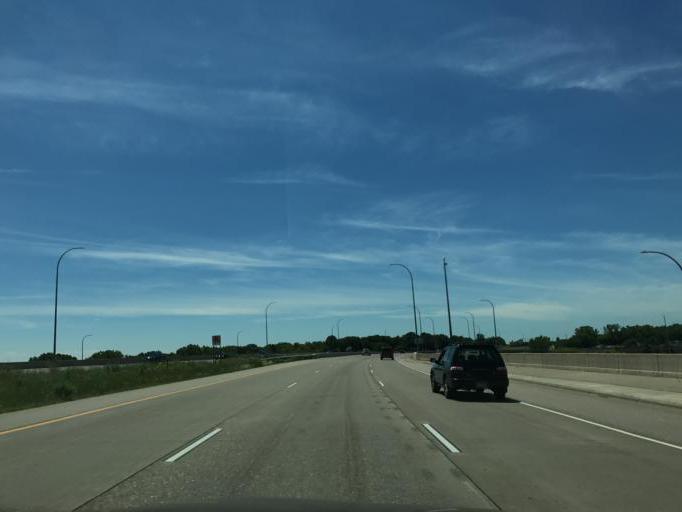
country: US
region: Minnesota
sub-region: Hennepin County
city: Osseo
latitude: 45.1077
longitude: -93.3923
